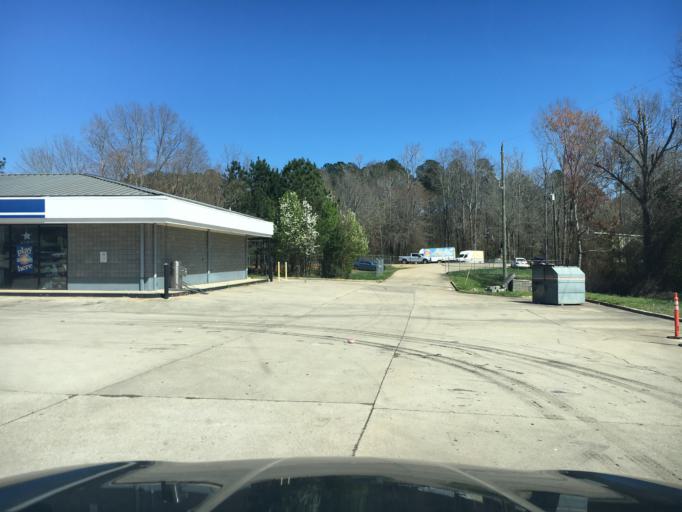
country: US
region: Georgia
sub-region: Troup County
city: La Grange
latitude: 33.0037
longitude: -85.0156
